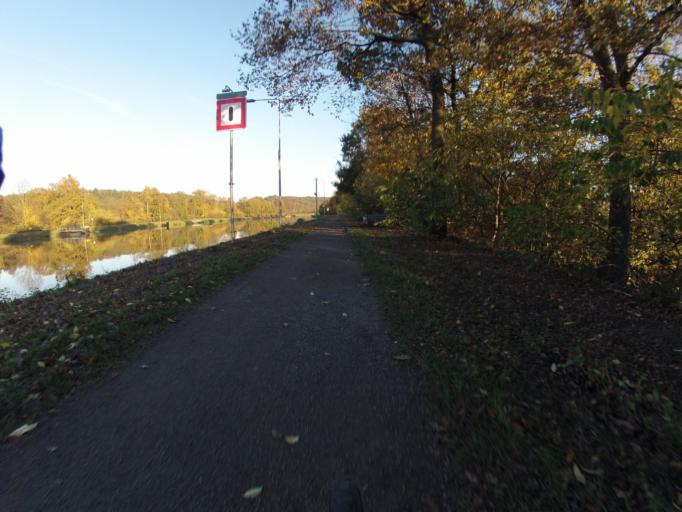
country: DE
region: North Rhine-Westphalia
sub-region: Regierungsbezirk Munster
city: Horstel
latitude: 52.2770
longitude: 7.5933
